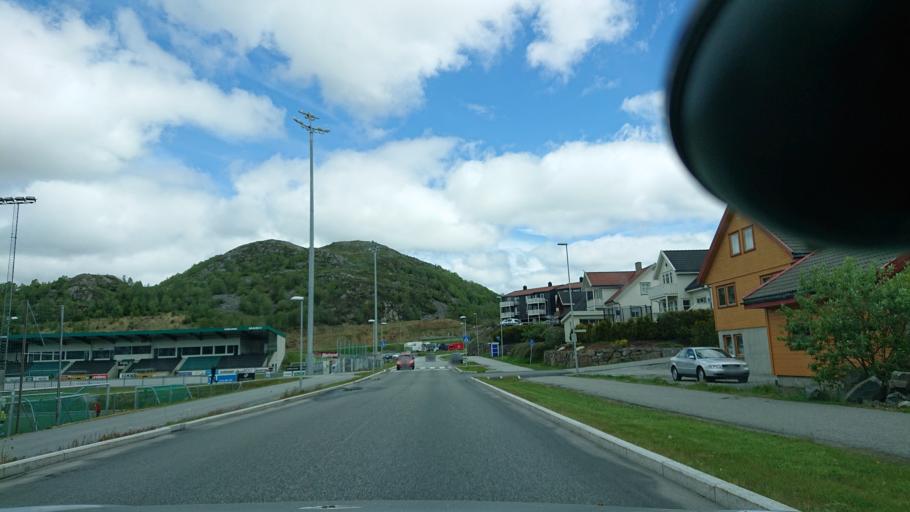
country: NO
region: Rogaland
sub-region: Gjesdal
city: Algard
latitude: 58.7740
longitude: 5.8672
